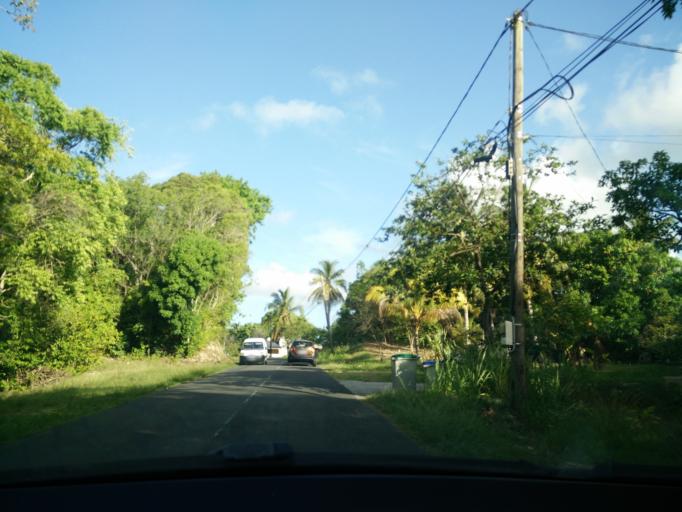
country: GP
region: Guadeloupe
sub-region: Guadeloupe
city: Sainte-Anne
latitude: 16.2780
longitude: -61.4021
